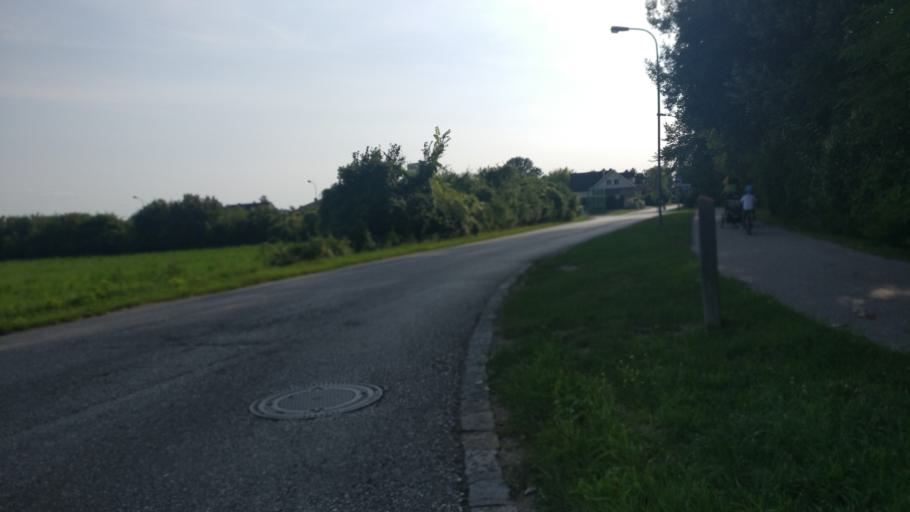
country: AT
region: Lower Austria
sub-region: Politischer Bezirk Baden
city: Ebreichsdorf
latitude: 47.9717
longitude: 16.4102
